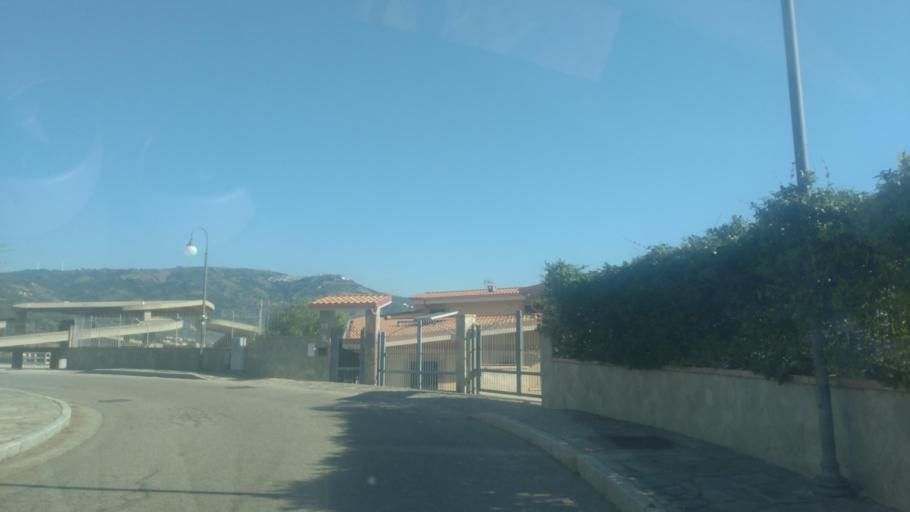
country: IT
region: Calabria
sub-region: Provincia di Catanzaro
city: Soverato Superiore
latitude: 38.7019
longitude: 16.5350
